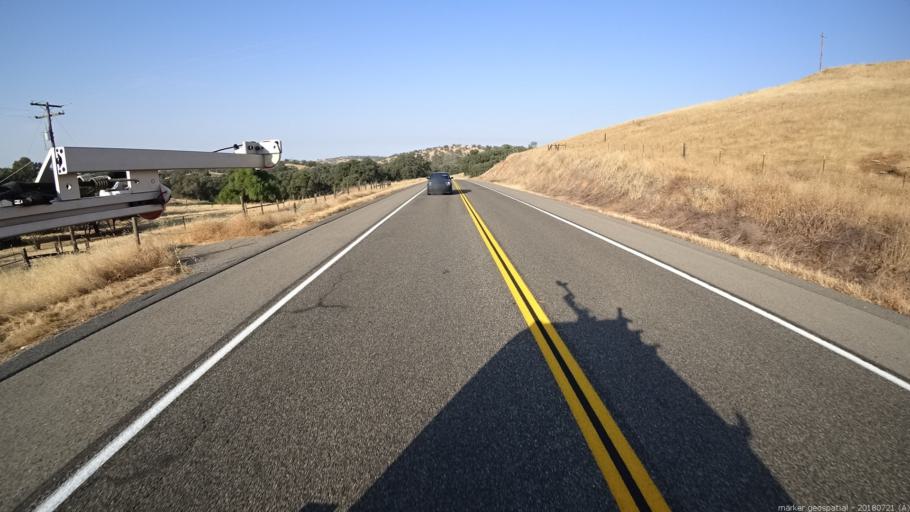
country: US
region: California
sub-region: Madera County
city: Yosemite Lakes
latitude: 37.1341
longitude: -119.6879
